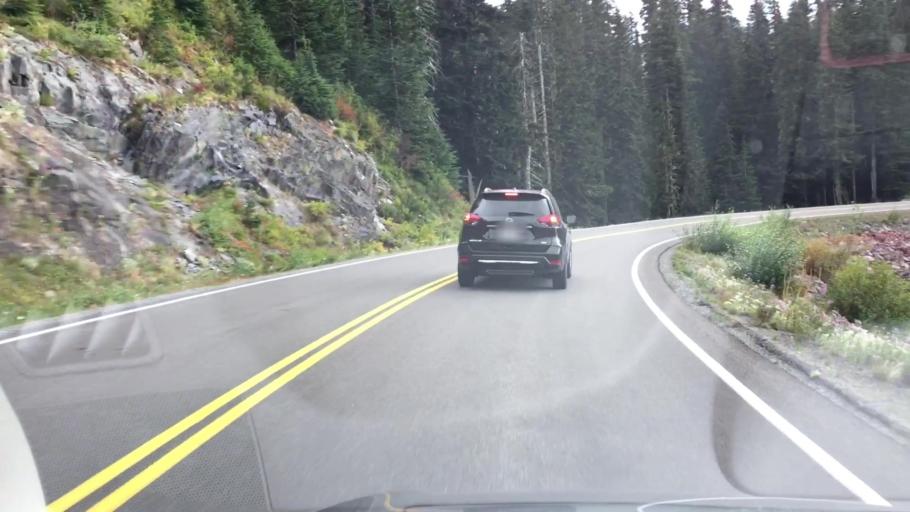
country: US
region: Washington
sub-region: Pierce County
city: Buckley
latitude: 46.7811
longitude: -121.7477
